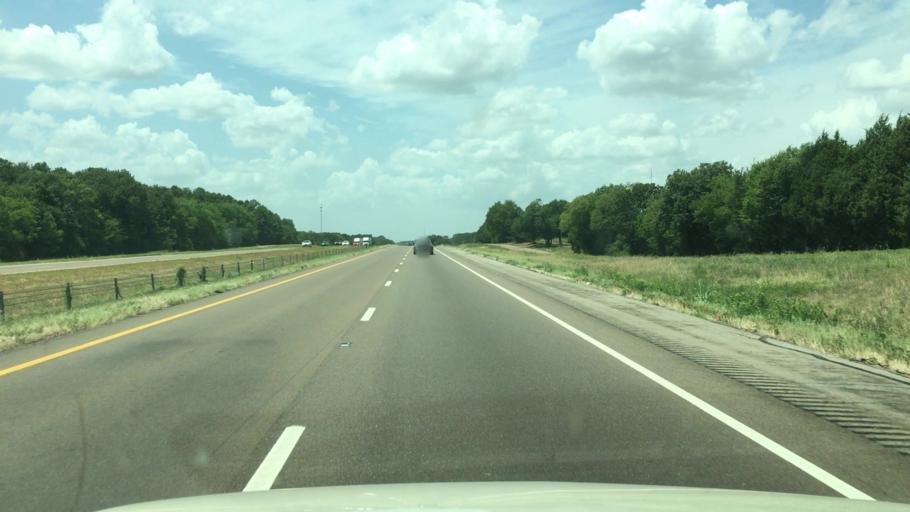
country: US
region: Texas
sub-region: Titus County
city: Mount Pleasant
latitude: 33.1597
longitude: -95.0833
